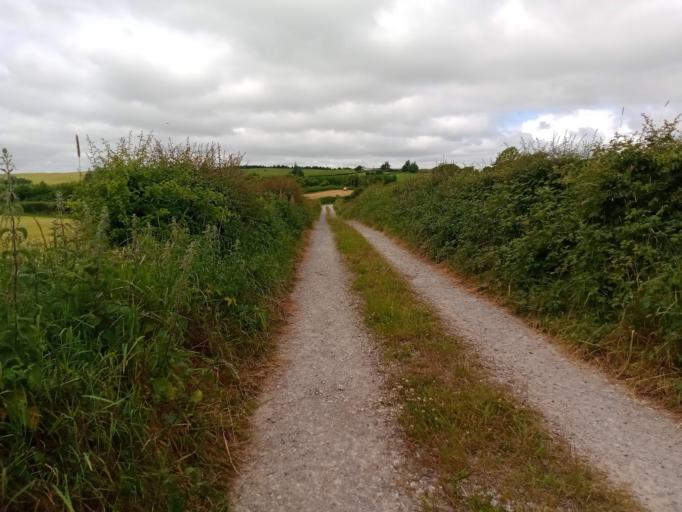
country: IE
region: Leinster
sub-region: Kilkenny
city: Ballyragget
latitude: 52.7939
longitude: -7.4619
